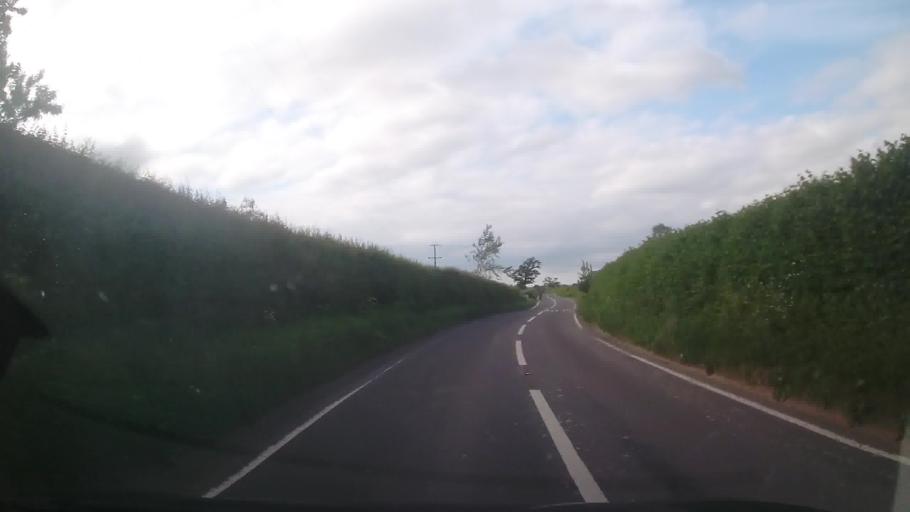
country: GB
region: England
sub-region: Shropshire
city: Petton
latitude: 52.8122
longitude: -2.7888
